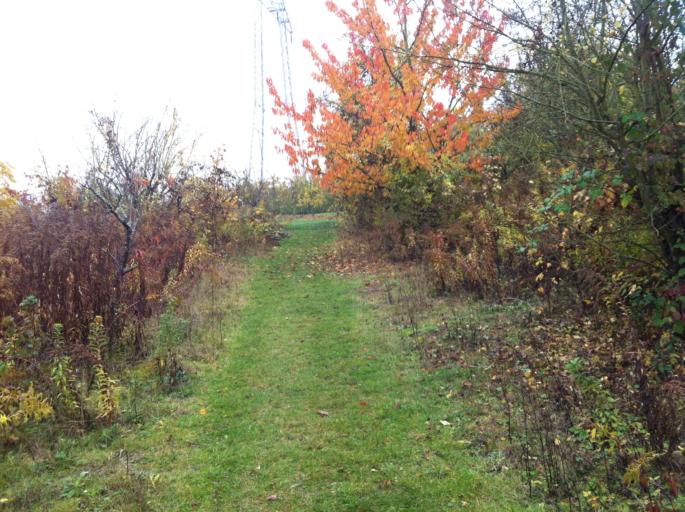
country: DE
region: Rheinland-Pfalz
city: Budenheim
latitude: 49.9953
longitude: 8.1920
